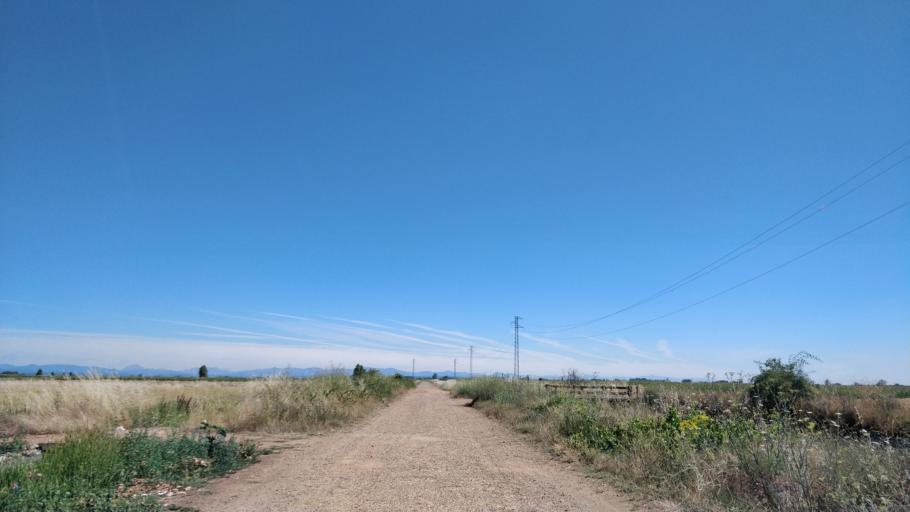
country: ES
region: Castille and Leon
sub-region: Provincia de Leon
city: Bustillo del Paramo
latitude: 42.4330
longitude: -5.8220
